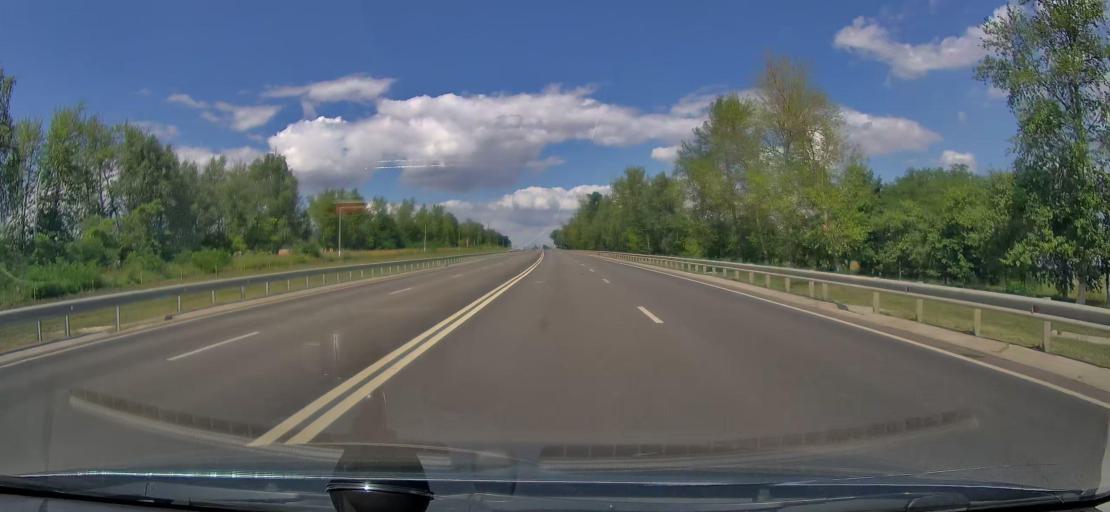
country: RU
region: Kursk
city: Zolotukhino
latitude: 51.9543
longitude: 36.3048
